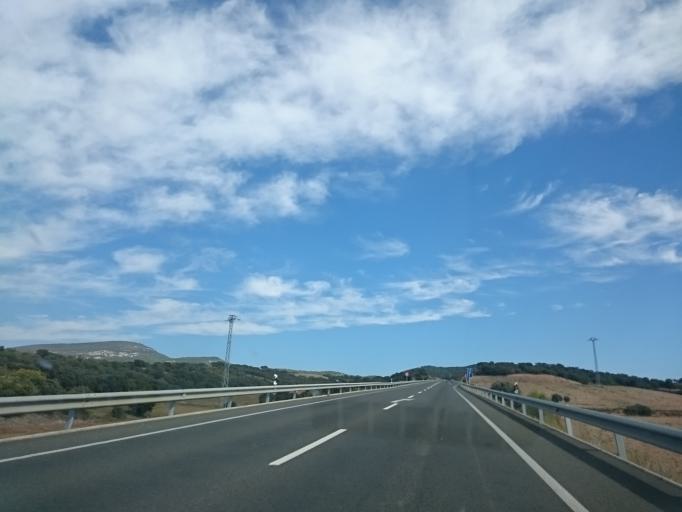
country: ES
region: Aragon
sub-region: Provincia de Huesca
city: Baells
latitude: 41.9550
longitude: 0.4682
